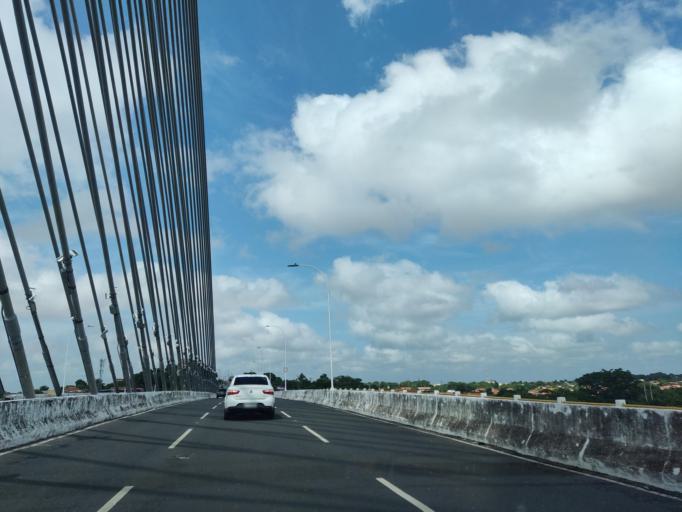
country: BR
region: Piaui
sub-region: Teresina
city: Teresina
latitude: -5.0699
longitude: -42.8026
